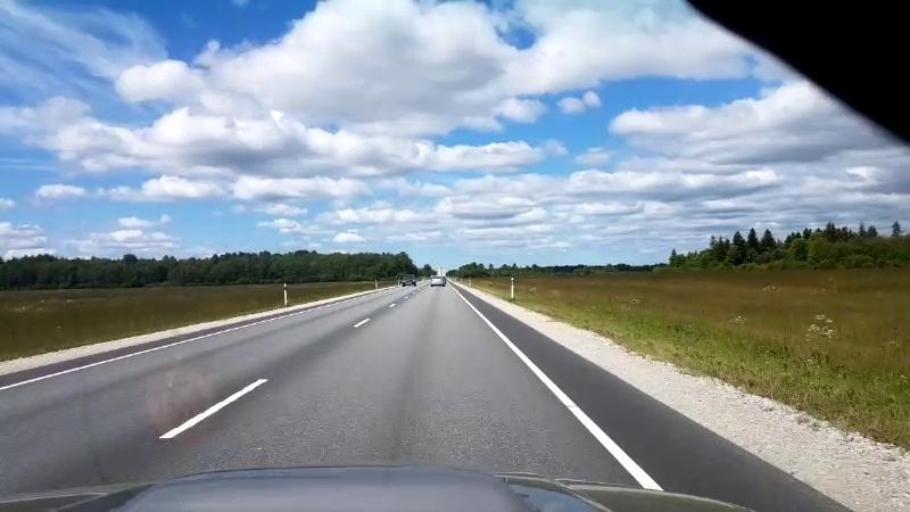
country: EE
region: Paernumaa
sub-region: Halinga vald
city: Parnu-Jaagupi
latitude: 58.6354
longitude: 24.4967
